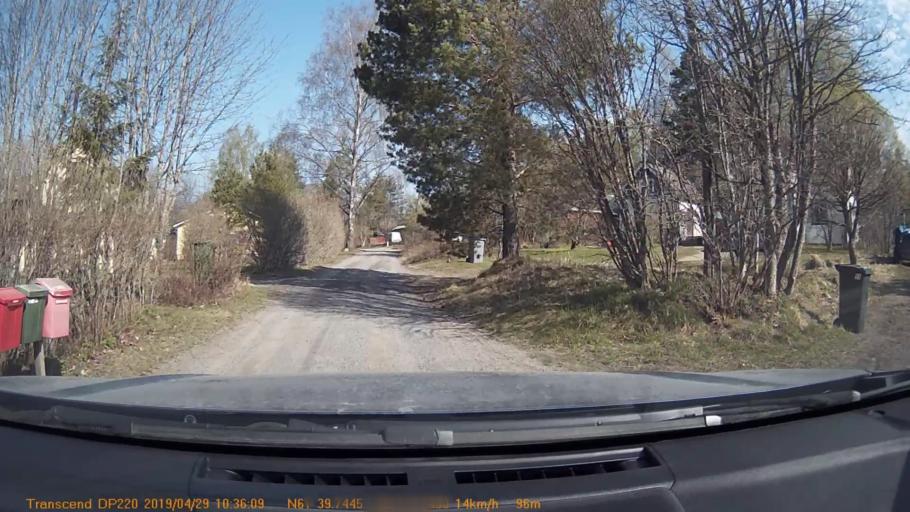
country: FI
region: Pirkanmaa
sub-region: Tampere
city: Haemeenkyroe
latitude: 61.6625
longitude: 23.2191
